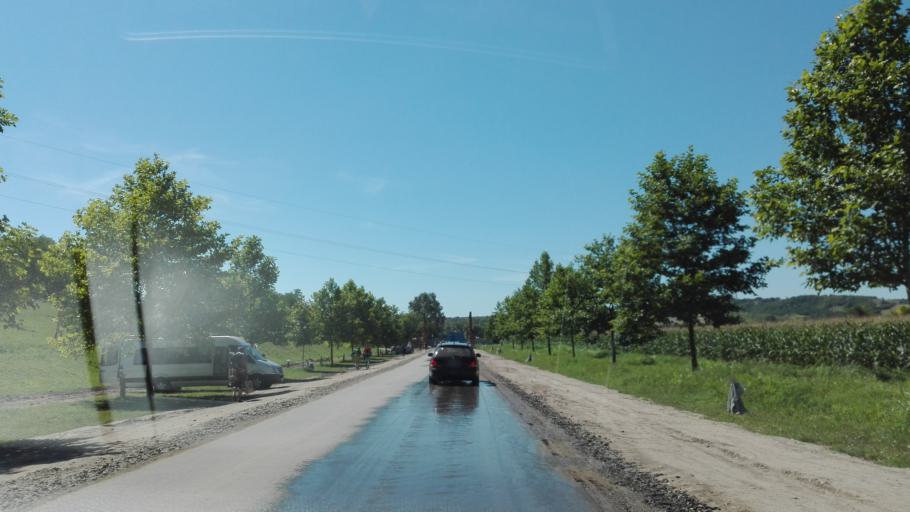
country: HU
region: Tolna
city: Ozora
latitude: 46.7576
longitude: 18.4353
